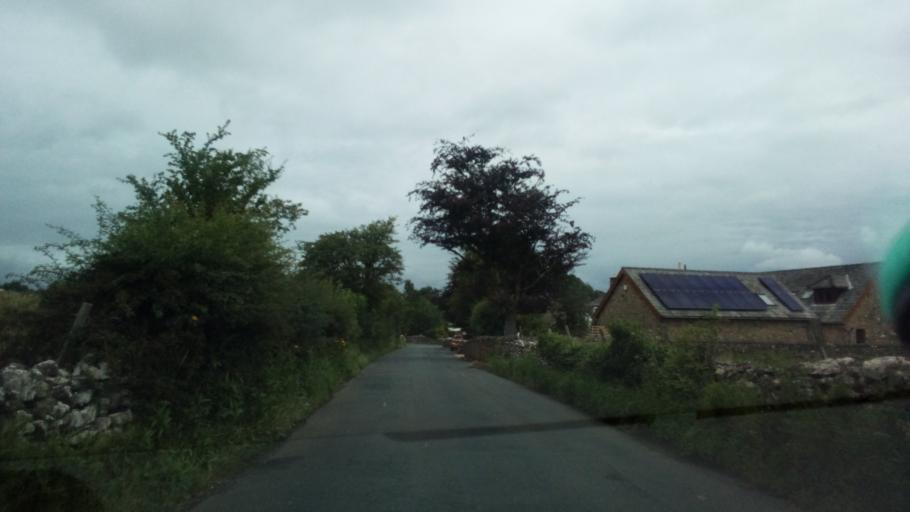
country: GB
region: England
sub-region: Cumbria
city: Kirkby Stephen
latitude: 54.4666
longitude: -2.3489
